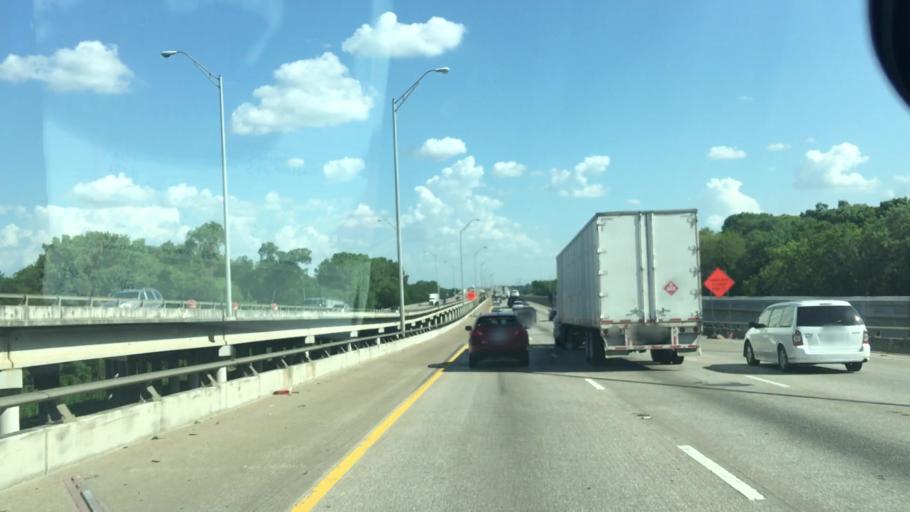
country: US
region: Texas
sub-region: Dallas County
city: Dallas
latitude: 32.7459
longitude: -96.7689
